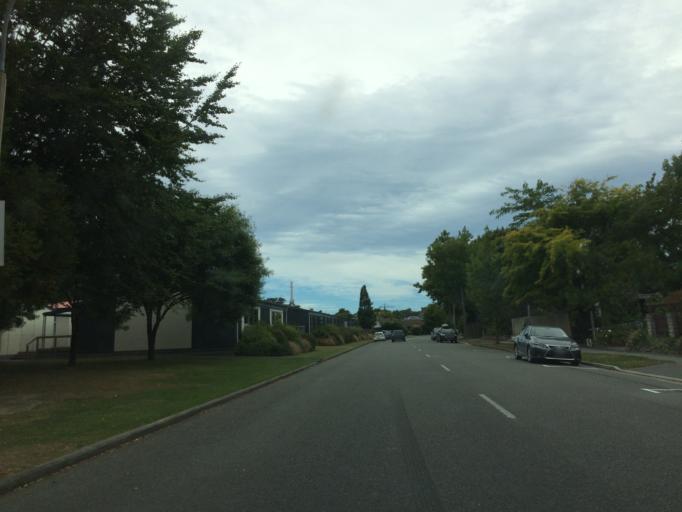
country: NZ
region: Canterbury
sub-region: Christchurch City
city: Christchurch
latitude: -43.5232
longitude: 172.5668
